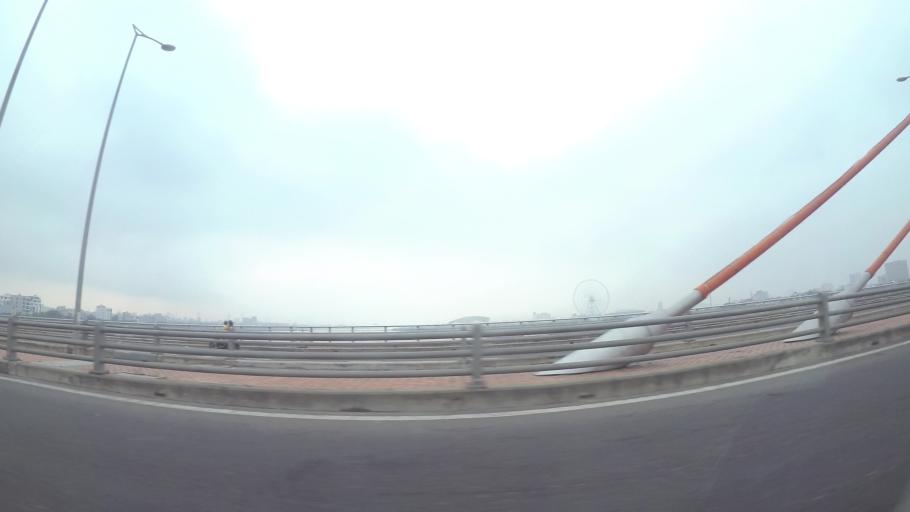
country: VN
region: Da Nang
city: Son Tra
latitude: 16.0505
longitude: 108.2303
